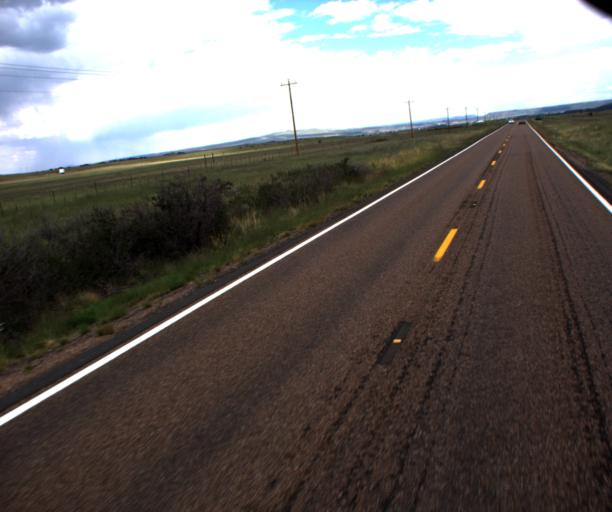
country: US
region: Arizona
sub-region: Apache County
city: Eagar
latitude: 34.1021
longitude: -109.3749
